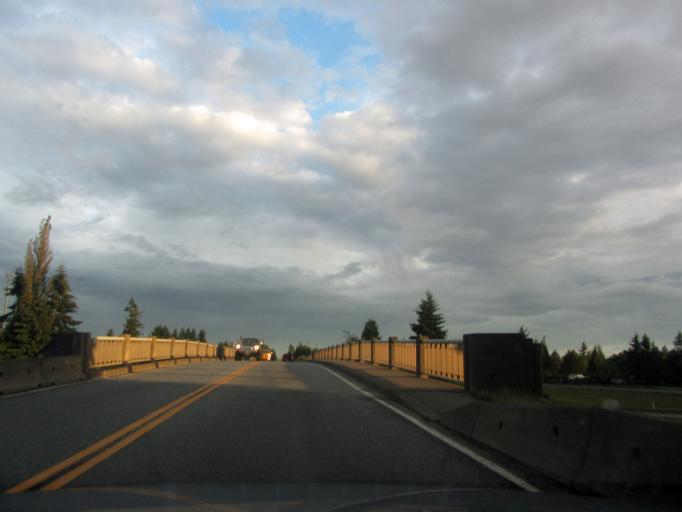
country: CA
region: British Columbia
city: Langley
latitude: 49.1369
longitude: -122.5813
